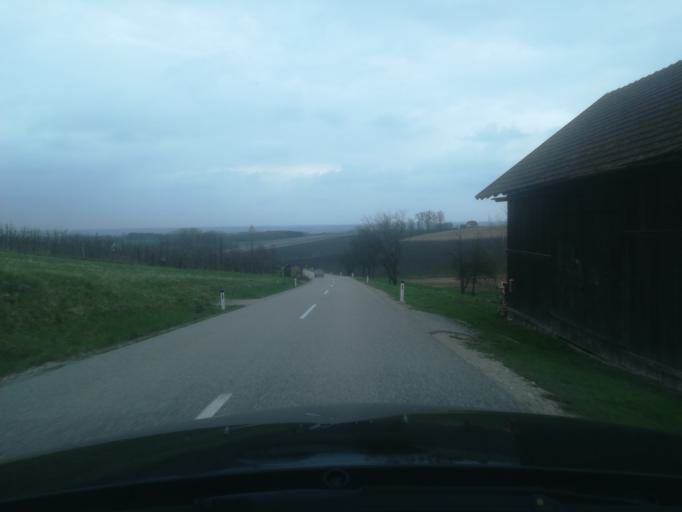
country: AT
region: Upper Austria
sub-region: Wels-Land
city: Buchkirchen
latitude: 48.2426
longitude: 14.0548
